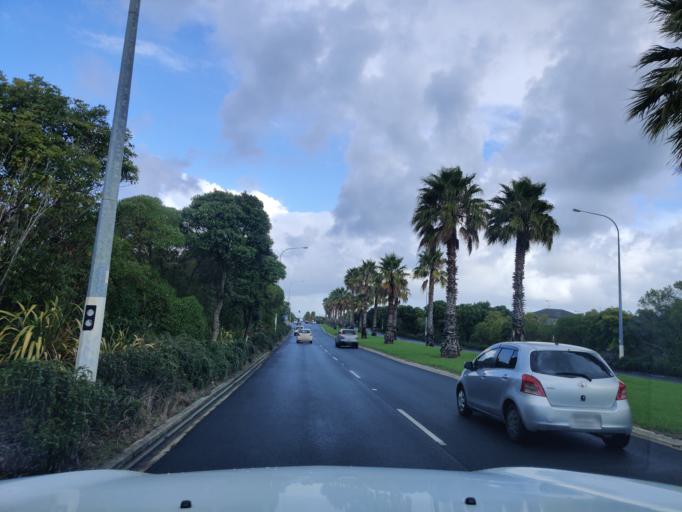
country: NZ
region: Auckland
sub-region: Auckland
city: Pakuranga
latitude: -36.9393
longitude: 174.9092
